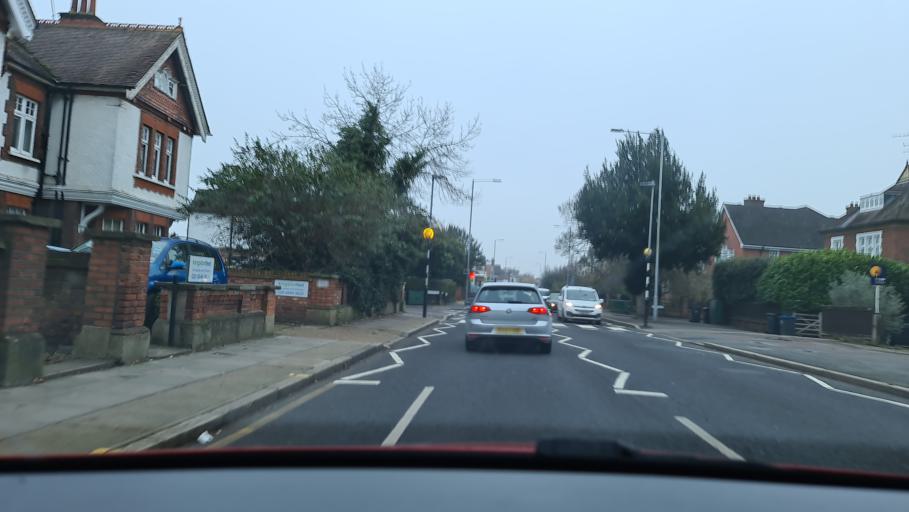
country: GB
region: England
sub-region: Greater London
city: Kingston upon Thames
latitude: 51.4209
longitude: -0.3023
